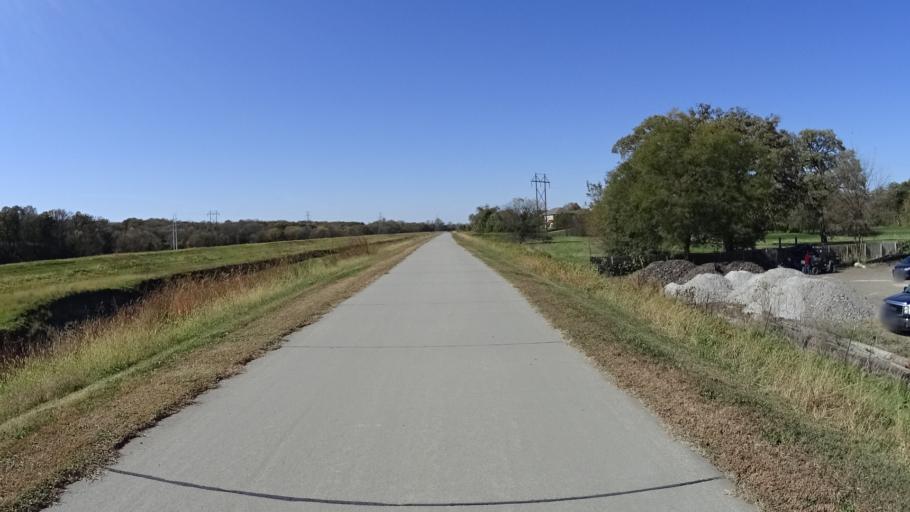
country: US
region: Nebraska
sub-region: Sarpy County
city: Papillion
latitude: 41.1514
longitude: -95.9951
